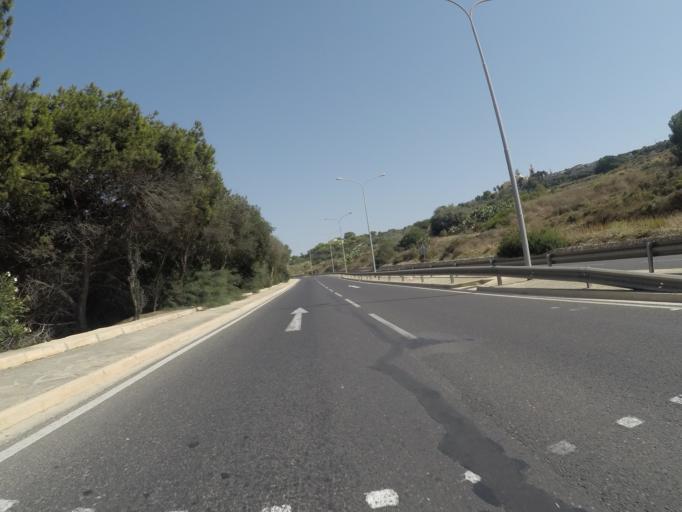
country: MT
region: Saint Paul's Bay
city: San Pawl il-Bahar
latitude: 35.9443
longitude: 14.3896
